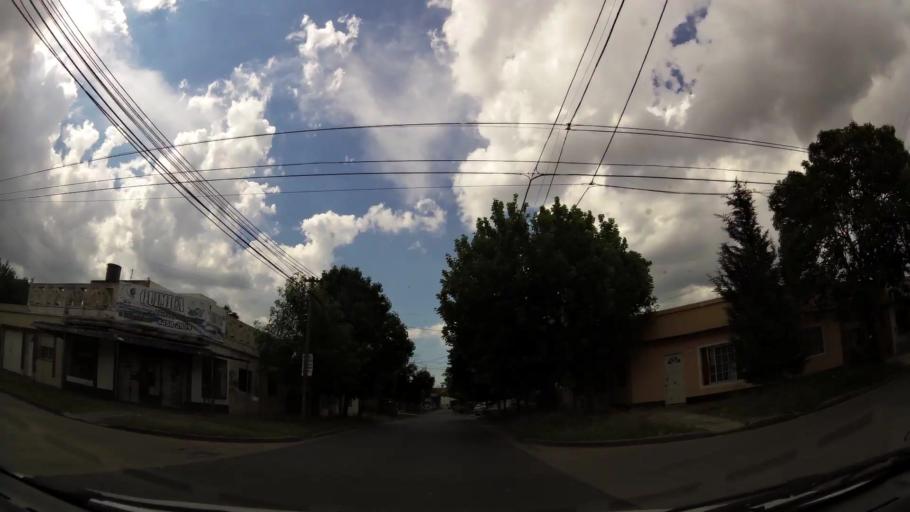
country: AR
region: Buenos Aires
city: Ituzaingo
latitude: -34.6410
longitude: -58.6627
